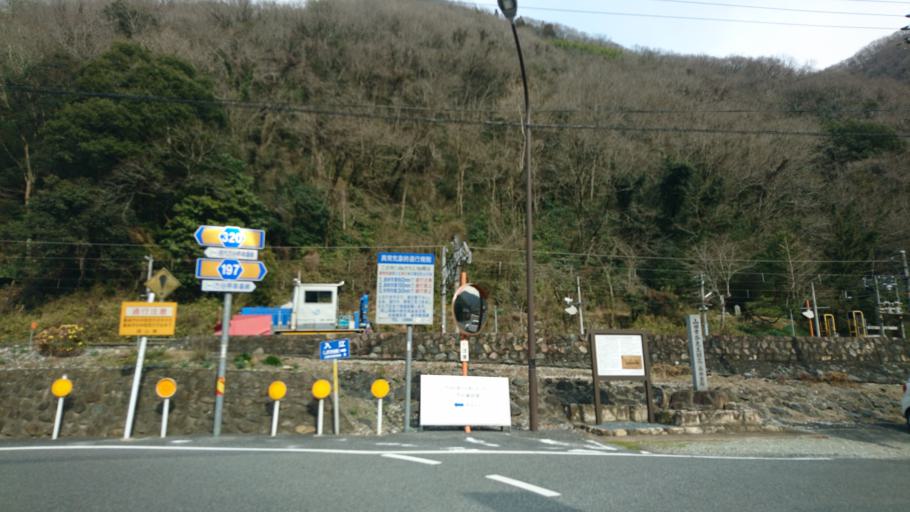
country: JP
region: Okayama
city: Takahashi
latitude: 34.8765
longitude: 133.5559
